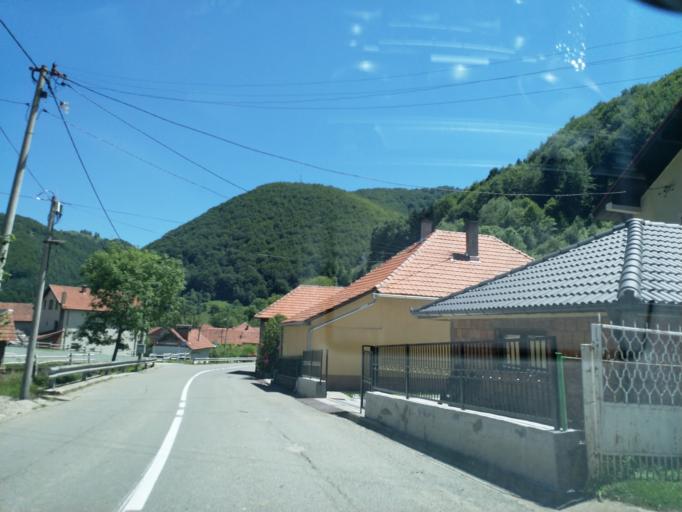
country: XK
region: Mitrovica
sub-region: Komuna e Leposaviqit
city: Leposaviq
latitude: 43.3024
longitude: 20.8811
